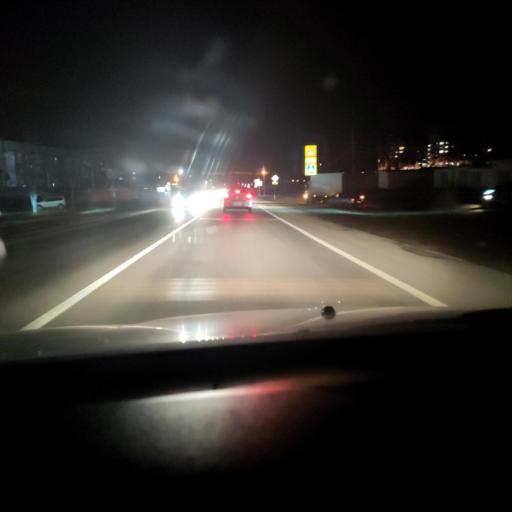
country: RU
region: Samara
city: Volzhskiy
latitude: 53.4393
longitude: 50.1241
